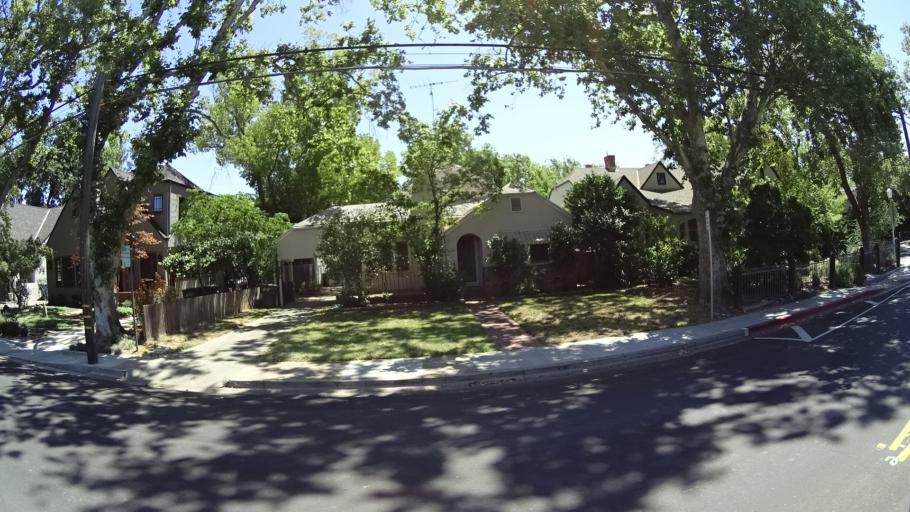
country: US
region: California
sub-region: Sacramento County
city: Sacramento
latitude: 38.5510
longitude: -121.4836
